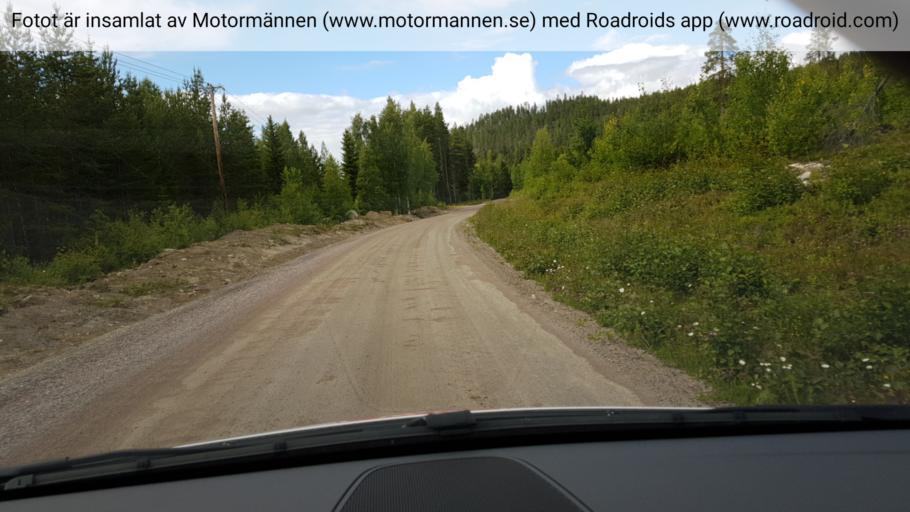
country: SE
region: Jaemtland
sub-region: Stroemsunds Kommun
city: Stroemsund
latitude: 63.9865
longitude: 16.0081
